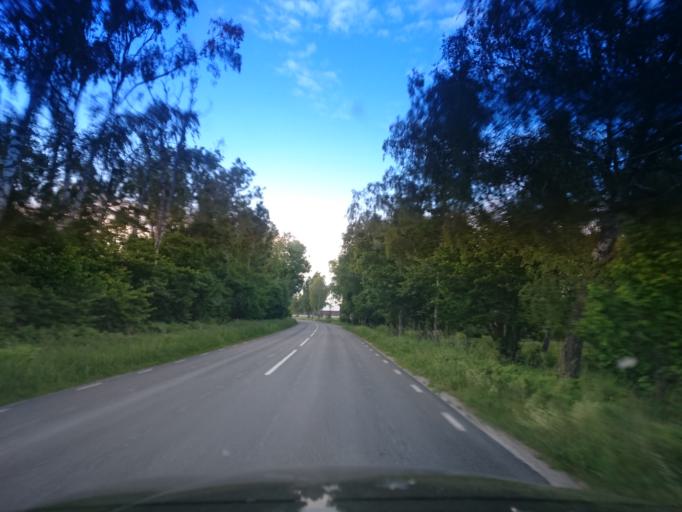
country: SE
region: Gotland
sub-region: Gotland
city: Hemse
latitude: 57.3165
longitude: 18.3848
